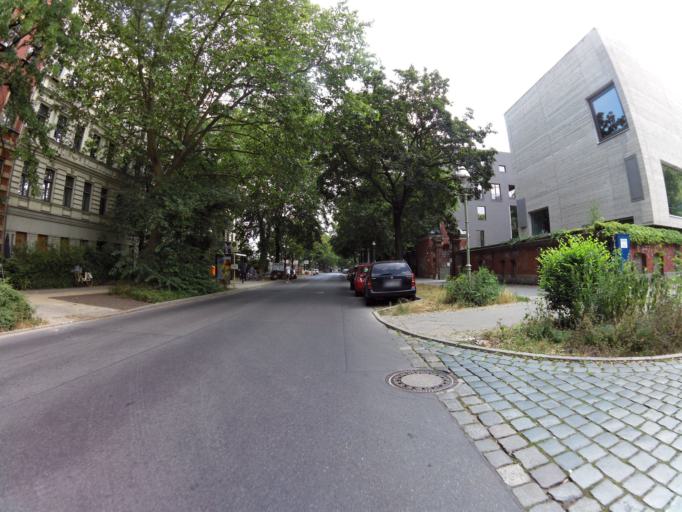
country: DE
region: Berlin
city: Wedding Bezirk
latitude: 52.5334
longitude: 13.3596
